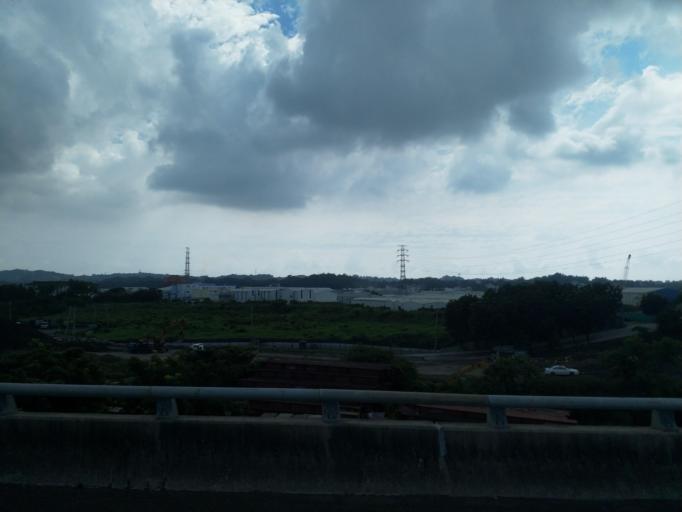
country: TW
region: Taiwan
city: Fengshan
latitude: 22.6900
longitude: 120.3571
